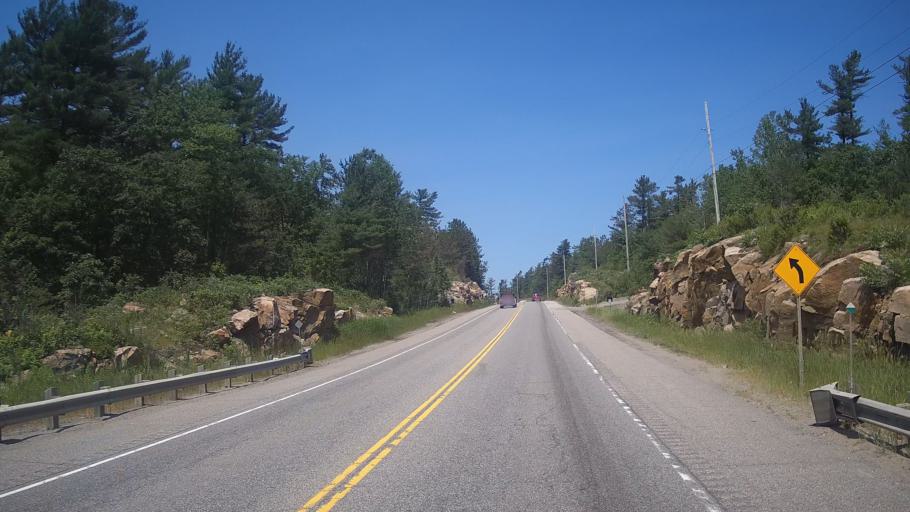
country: CA
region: Ontario
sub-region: Parry Sound District
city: Parry Sound
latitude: 45.6461
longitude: -80.3999
